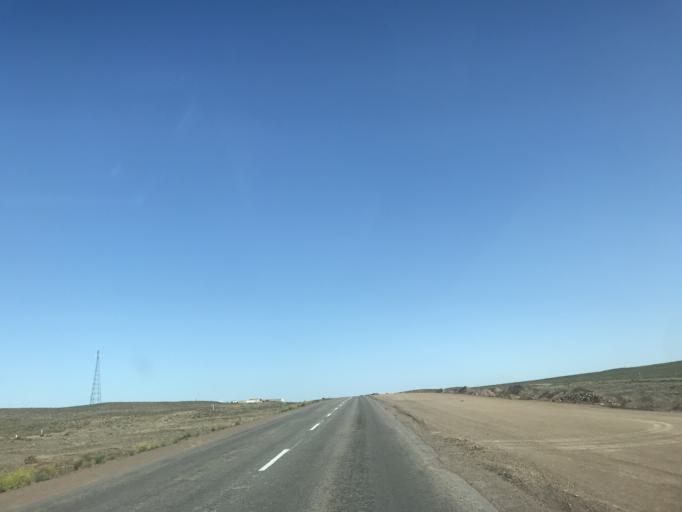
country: KZ
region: Zhambyl
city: Mynaral
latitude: 45.3305
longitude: 73.7269
